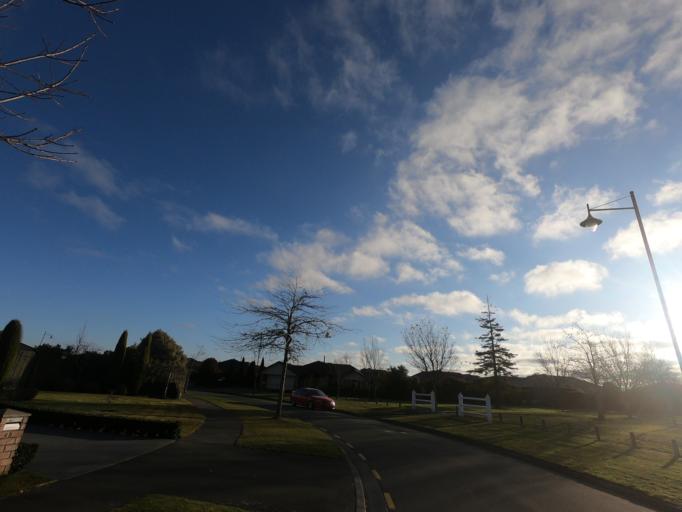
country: NZ
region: Canterbury
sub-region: Selwyn District
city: Prebbleton
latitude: -43.5661
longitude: 172.5680
